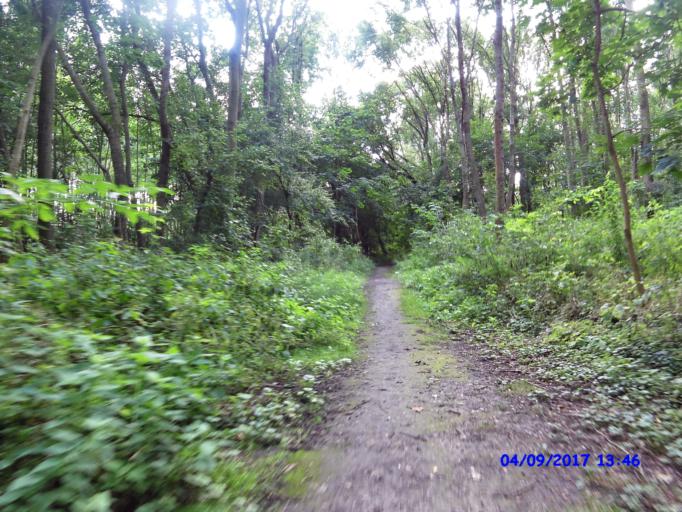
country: DE
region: Saxony
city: Taucha
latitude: 51.3531
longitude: 12.4721
